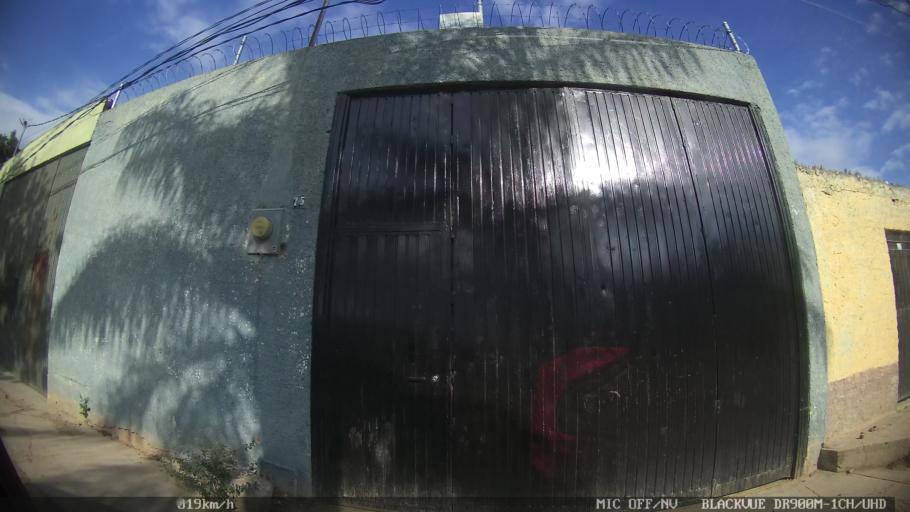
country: MX
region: Jalisco
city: Tonala
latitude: 20.6746
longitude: -103.2452
